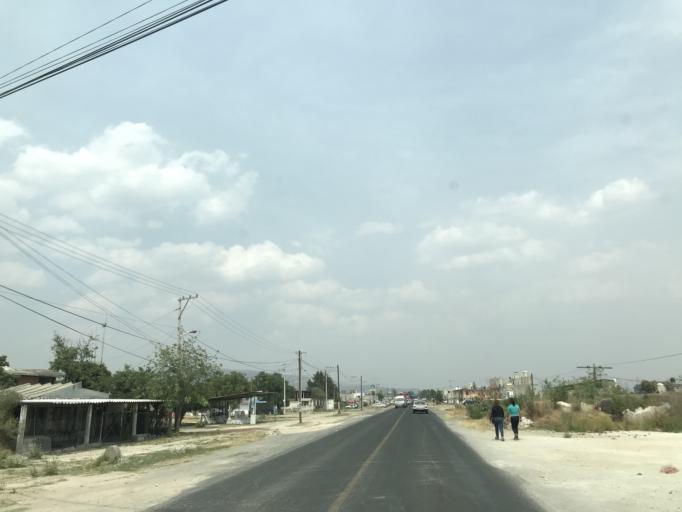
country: MX
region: Tlaxcala
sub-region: Ixtacuixtla de Mariano Matamoros
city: Santa Justina Ecatepec
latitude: 19.3123
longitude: -98.3412
